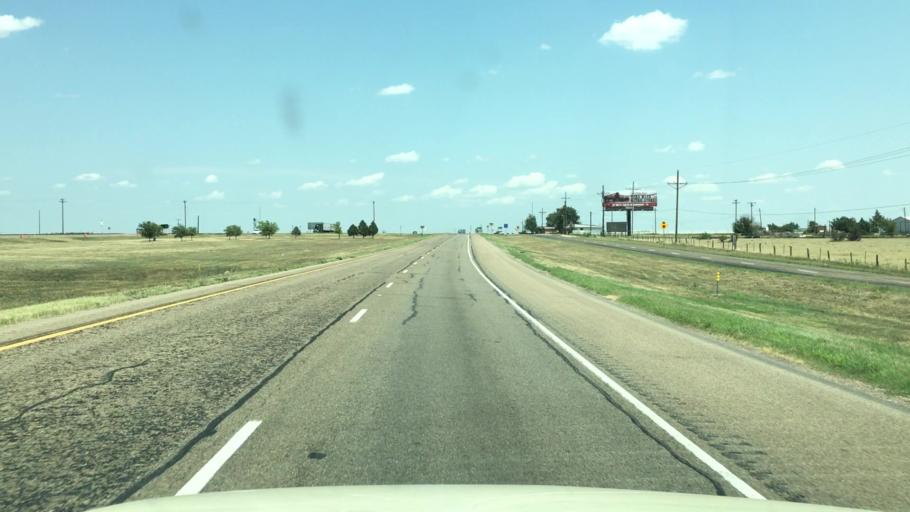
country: US
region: Texas
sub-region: Potter County
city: Amarillo
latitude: 35.1928
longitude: -101.6925
